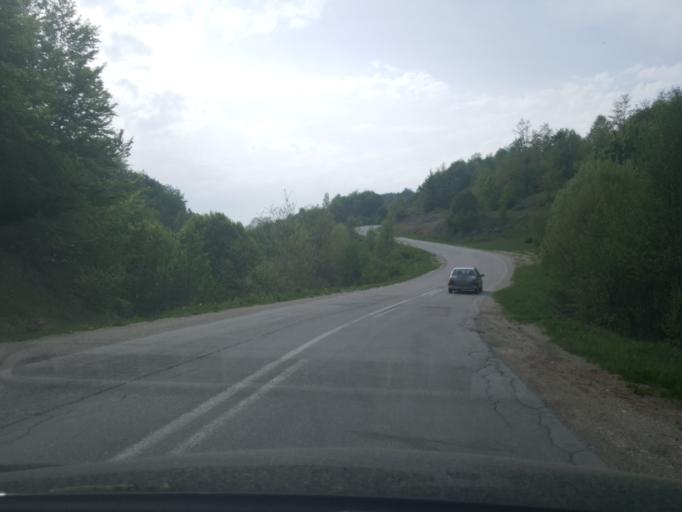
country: RS
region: Central Serbia
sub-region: Zlatiborski Okrug
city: Bajina Basta
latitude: 44.1011
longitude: 19.6719
